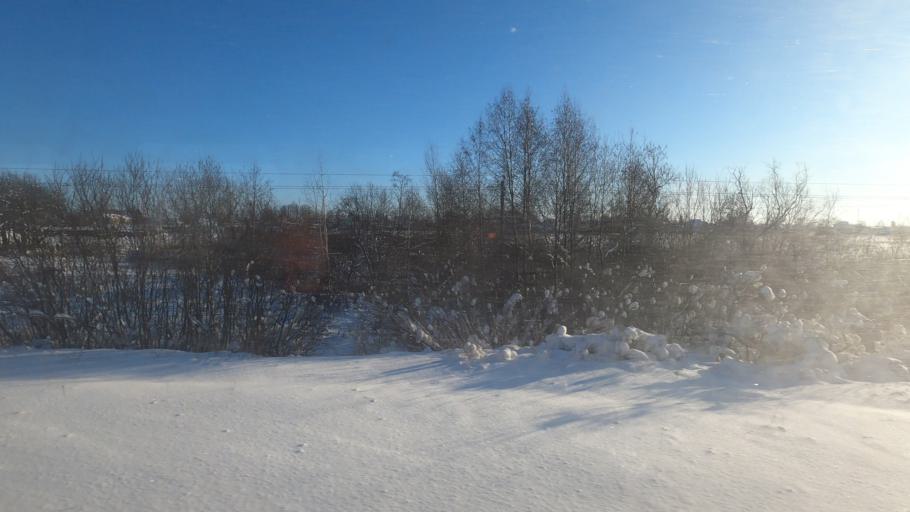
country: RU
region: Moskovskaya
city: Orud'yevo
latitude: 56.4413
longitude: 37.5130
